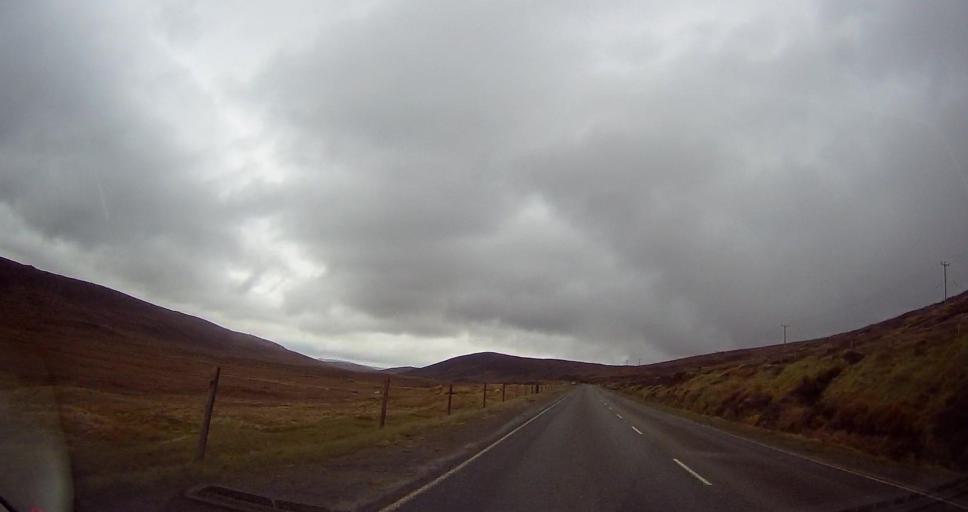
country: GB
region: Scotland
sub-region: Shetland Islands
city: Lerwick
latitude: 60.2903
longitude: -1.2405
